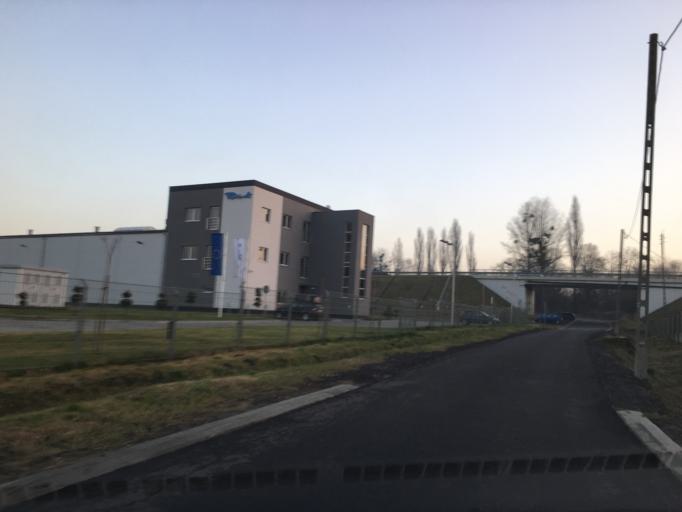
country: PL
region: Silesian Voivodeship
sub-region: Powiat tarnogorski
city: Radzionkow
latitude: 50.3692
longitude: 18.8871
